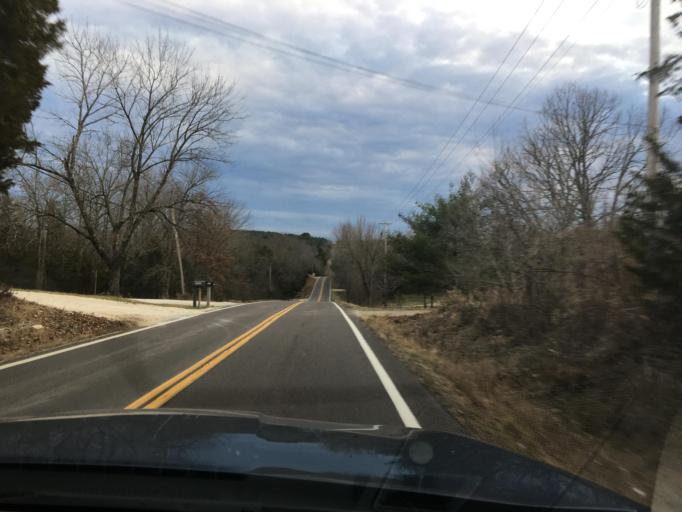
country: US
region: Missouri
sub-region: Jefferson County
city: De Soto
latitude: 38.0976
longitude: -90.5615
